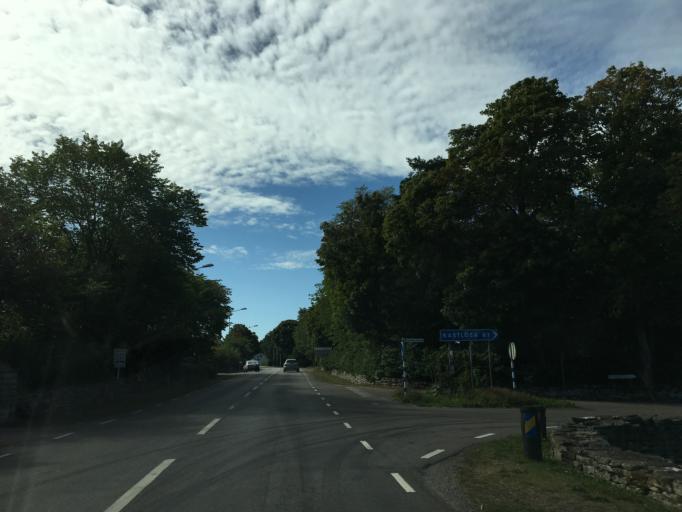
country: SE
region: Kalmar
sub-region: Morbylanga Kommun
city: Moerbylanga
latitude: 56.4580
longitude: 16.4299
